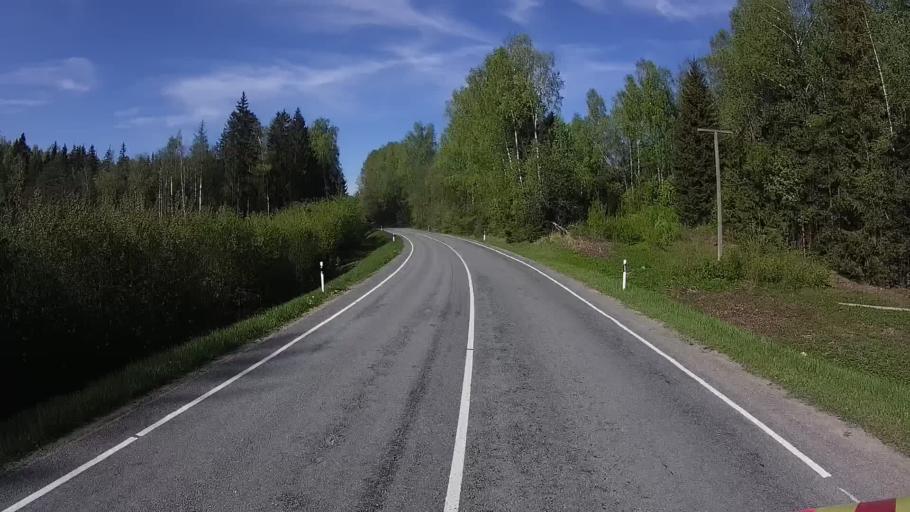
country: EE
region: Vorumaa
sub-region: Antsla vald
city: Vana-Antsla
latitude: 57.9725
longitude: 26.4643
